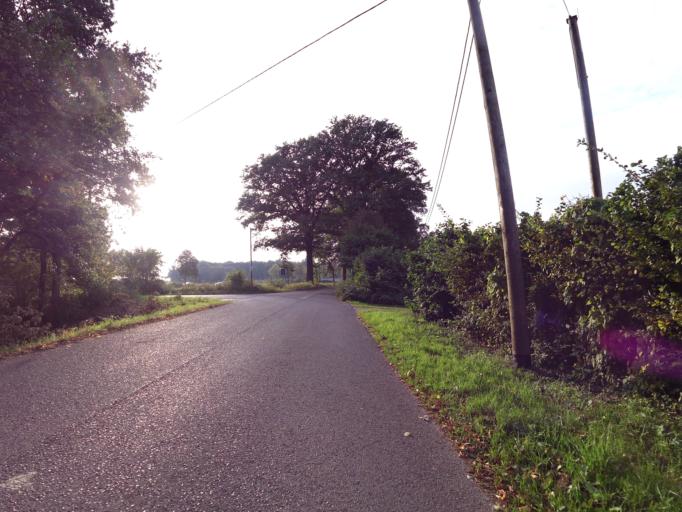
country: DE
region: North Rhine-Westphalia
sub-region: Regierungsbezirk Munster
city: Isselburg
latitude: 51.8114
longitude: 6.4882
